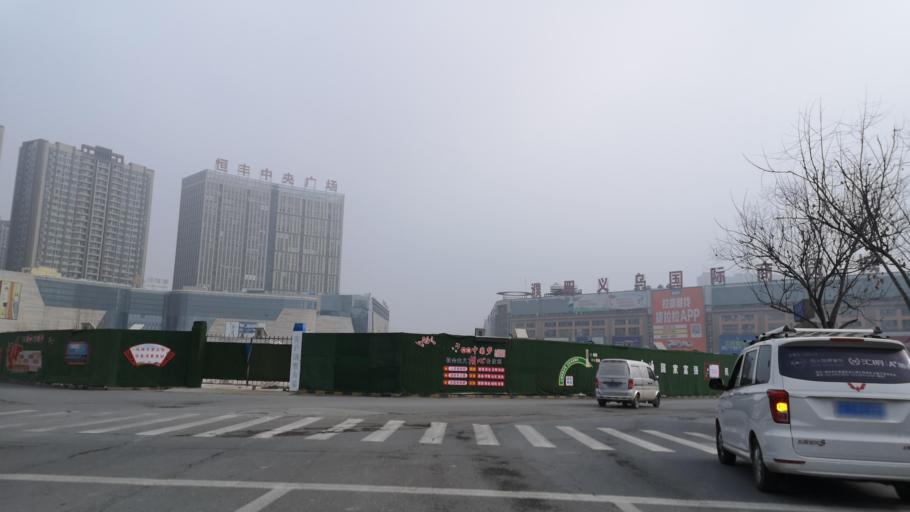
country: CN
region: Henan Sheng
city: Zhongyuanlu
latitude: 35.7756
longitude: 115.0525
